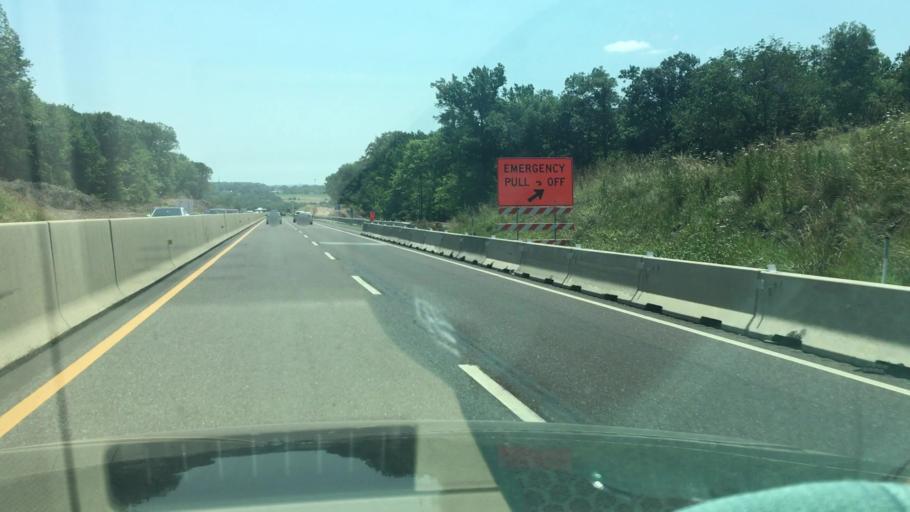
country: US
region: Pennsylvania
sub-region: Montgomery County
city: Telford
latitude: 40.3424
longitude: -75.3863
